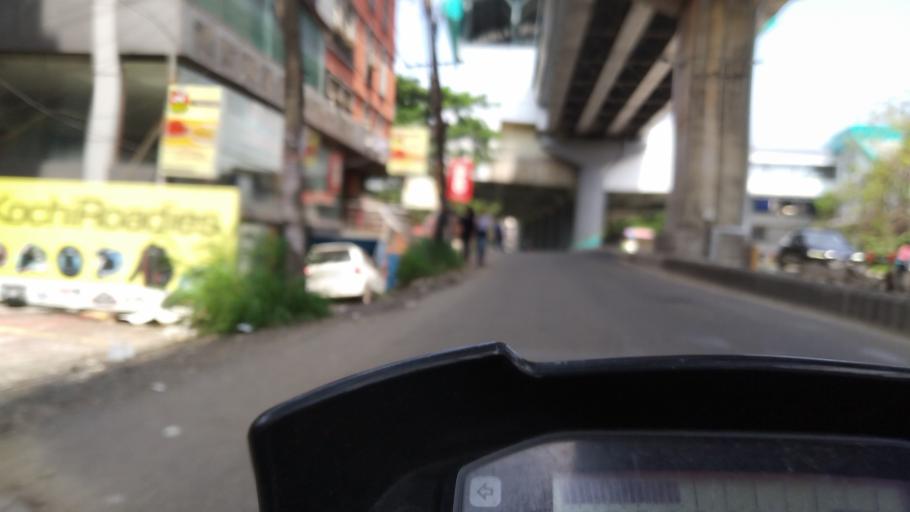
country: IN
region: Kerala
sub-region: Ernakulam
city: Cochin
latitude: 9.9663
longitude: 76.2972
